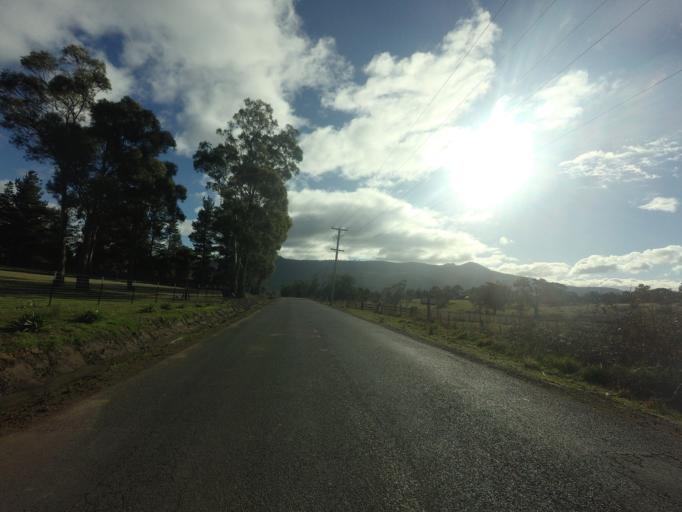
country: AU
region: Tasmania
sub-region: Derwent Valley
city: New Norfolk
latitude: -42.7878
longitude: 147.1202
